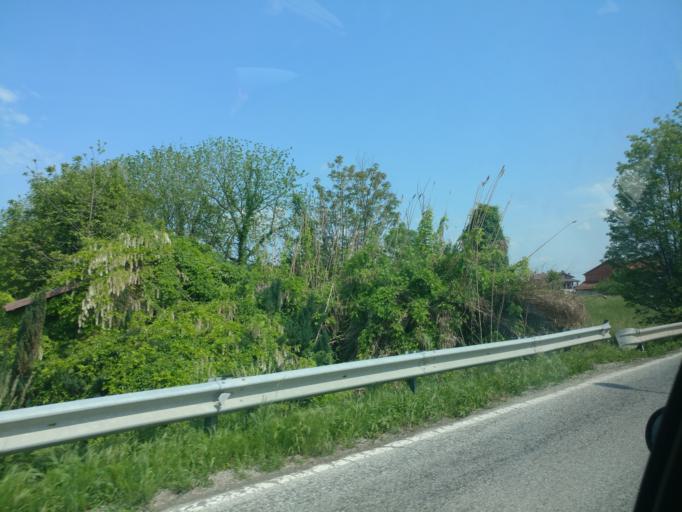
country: IT
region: Piedmont
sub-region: Provincia di Torino
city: Cavour
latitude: 44.7477
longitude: 7.4089
